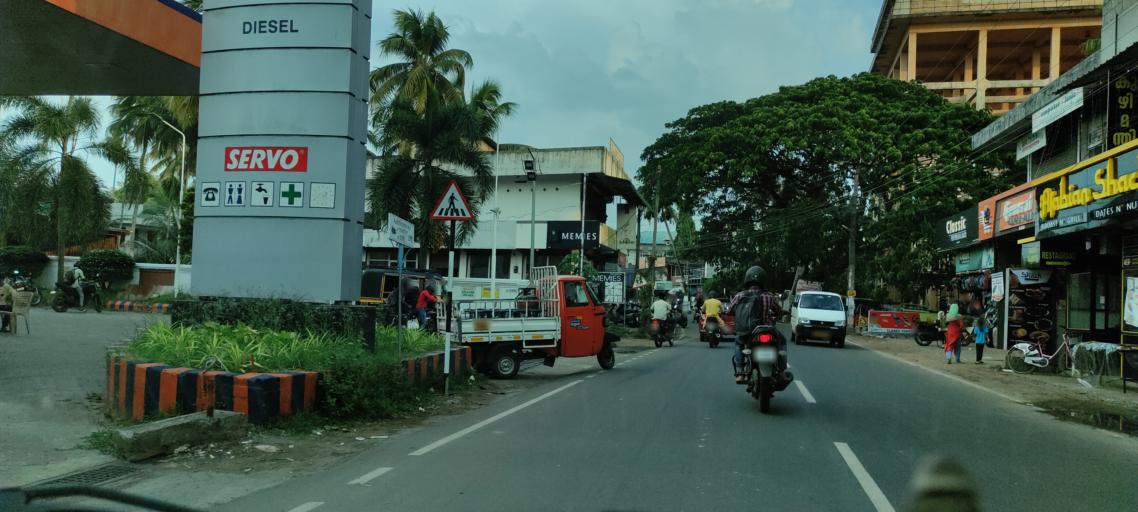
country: IN
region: Kerala
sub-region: Alappuzha
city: Arukutti
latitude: 9.8511
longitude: 76.3274
